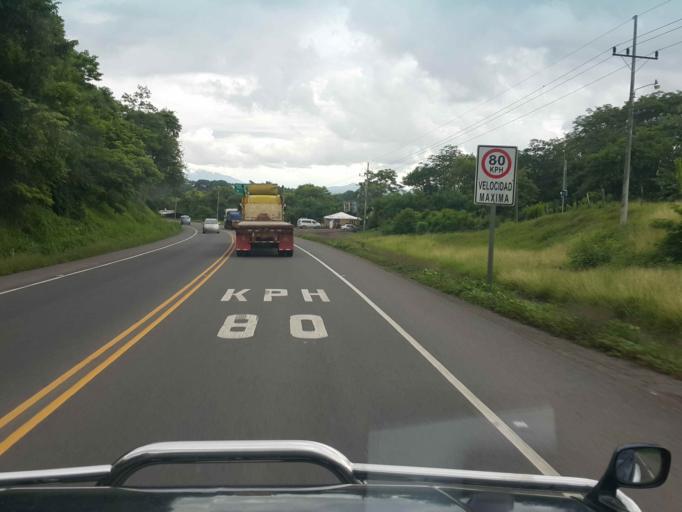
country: CR
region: Puntarenas
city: Esparza
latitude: 9.9161
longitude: -84.6827
